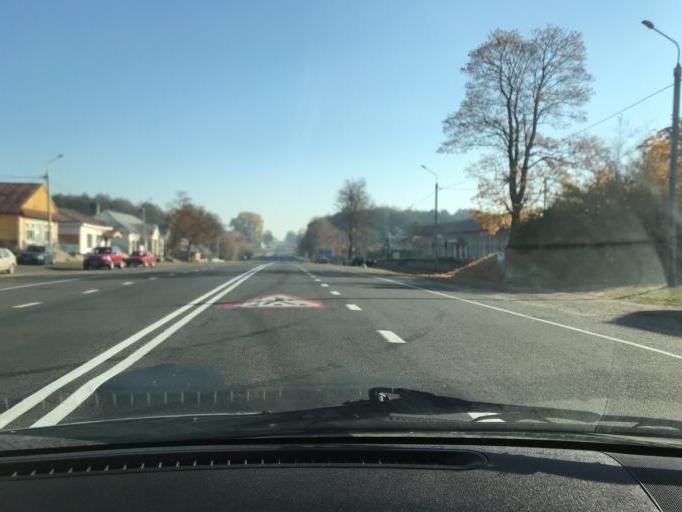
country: BY
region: Minsk
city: Klyetsk
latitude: 52.9631
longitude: 26.4684
